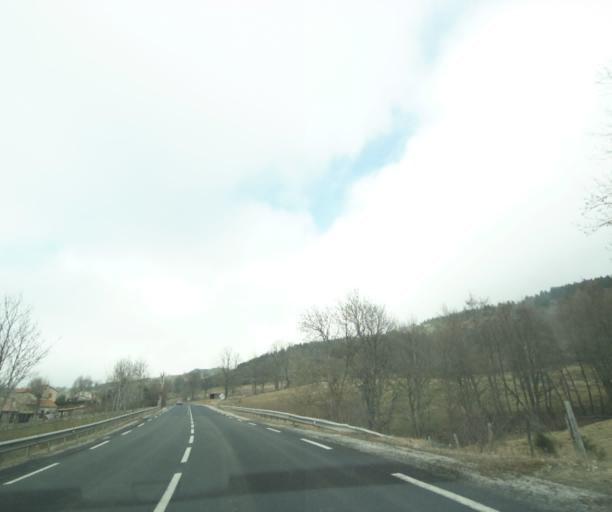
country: FR
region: Languedoc-Roussillon
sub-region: Departement de la Lozere
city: Langogne
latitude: 44.7568
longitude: 3.8910
